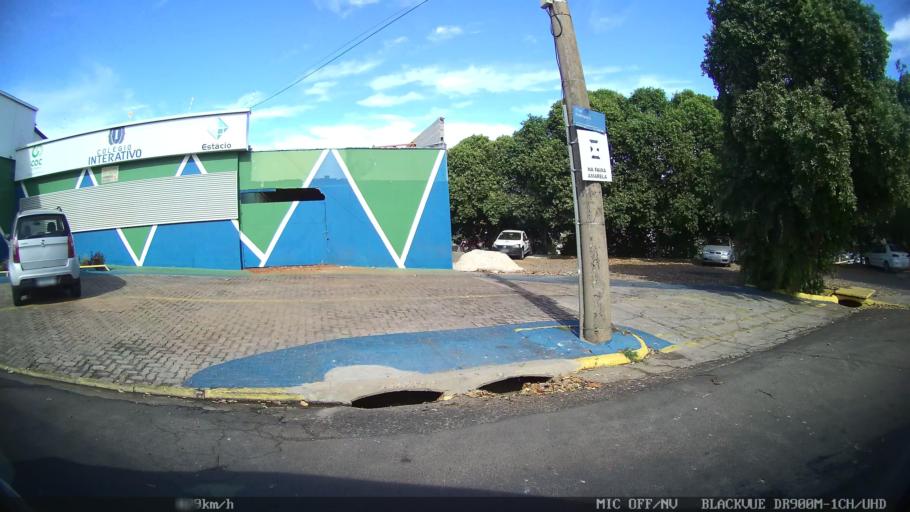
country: BR
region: Sao Paulo
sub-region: Catanduva
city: Catanduva
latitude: -21.1354
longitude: -48.9670
